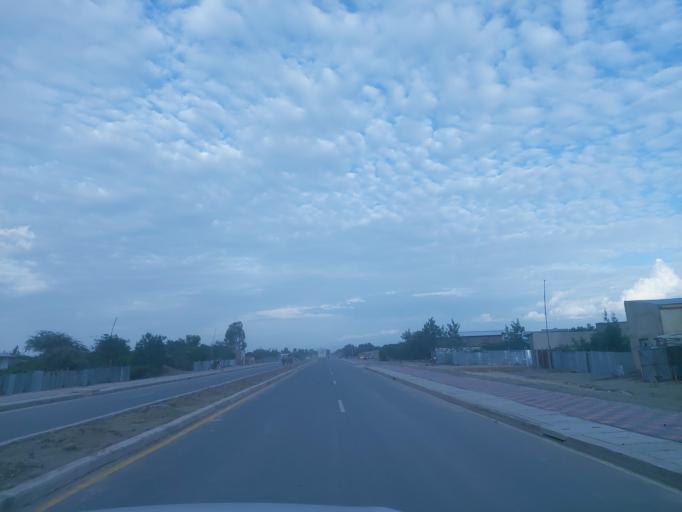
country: ET
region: Oromiya
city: Ziway
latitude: 8.1467
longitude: 38.8028
